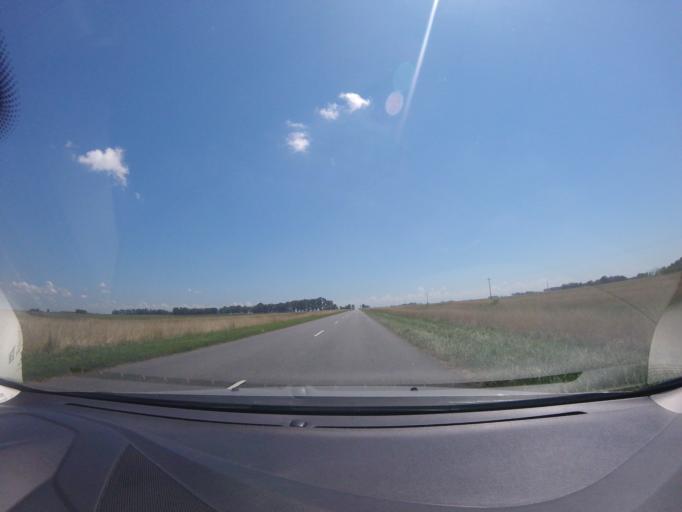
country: AR
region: Buenos Aires
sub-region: Partido de Rauch
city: Rauch
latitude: -36.5884
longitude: -59.0561
